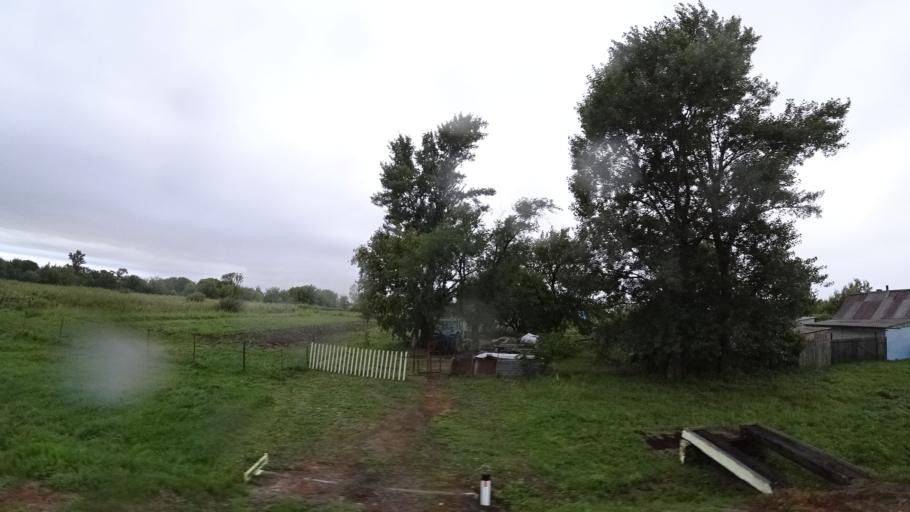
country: RU
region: Primorskiy
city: Chernigovka
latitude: 44.4069
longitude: 132.5299
